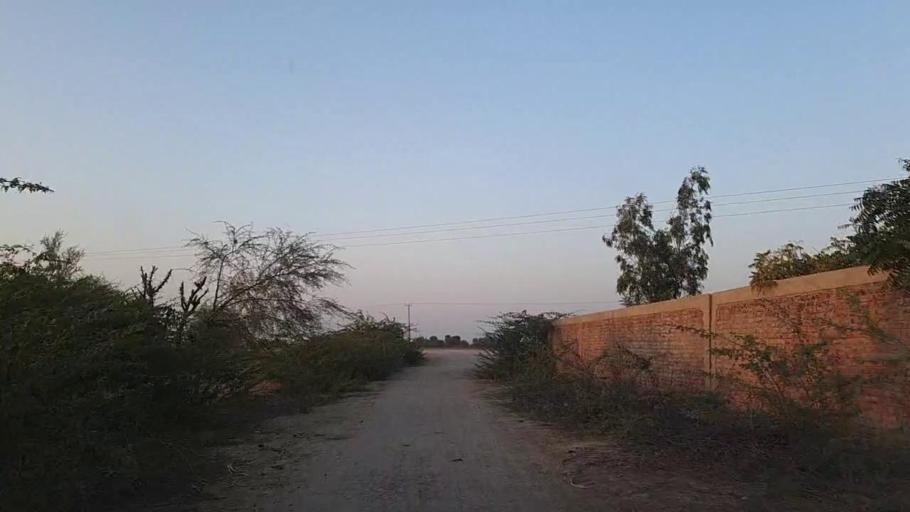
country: PK
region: Sindh
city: Naukot
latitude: 24.8842
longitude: 69.3537
